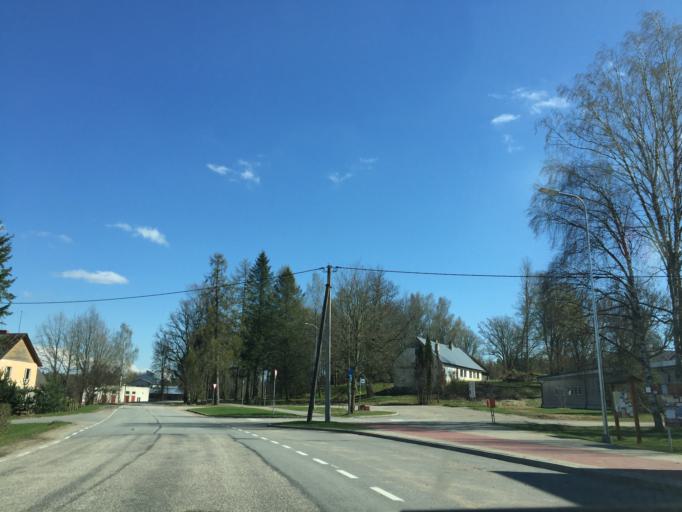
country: EE
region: Valgamaa
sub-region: Valga linn
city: Valga
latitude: 57.8551
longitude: 26.1173
